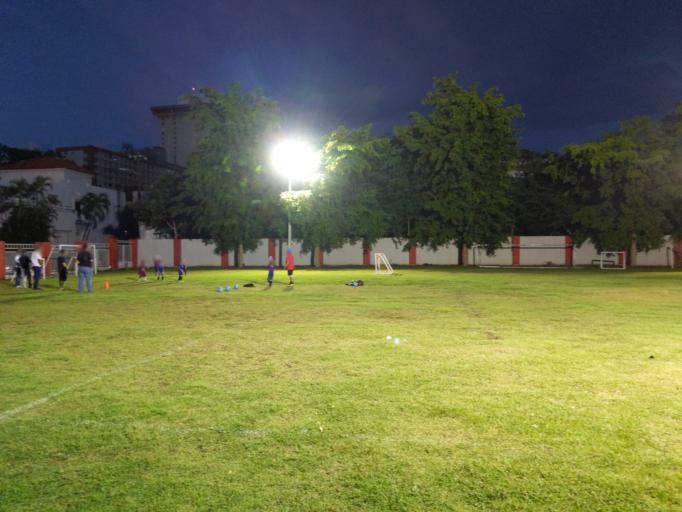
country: PR
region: San Juan
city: San Juan
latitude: 18.4513
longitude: -66.0889
